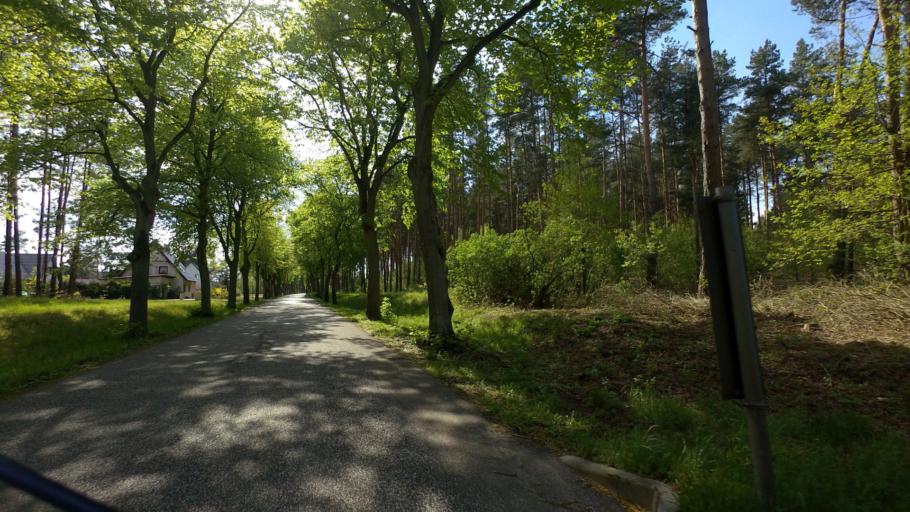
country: DE
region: Brandenburg
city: Templin
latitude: 52.9948
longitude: 13.5387
